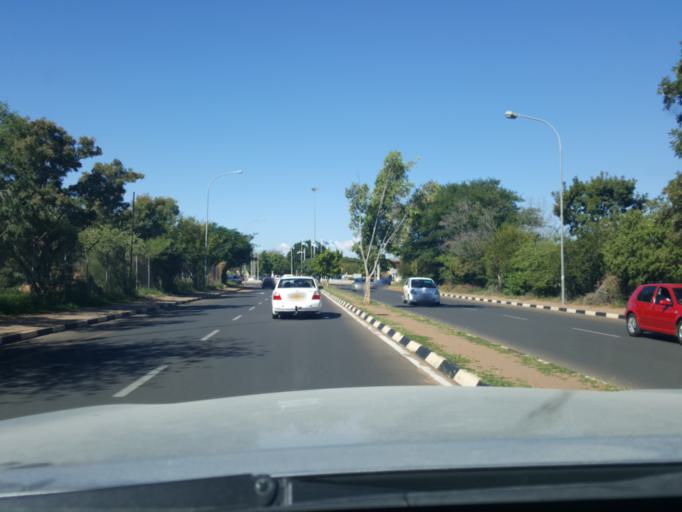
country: BW
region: South East
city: Gaborone
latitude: -24.6581
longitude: 25.9214
